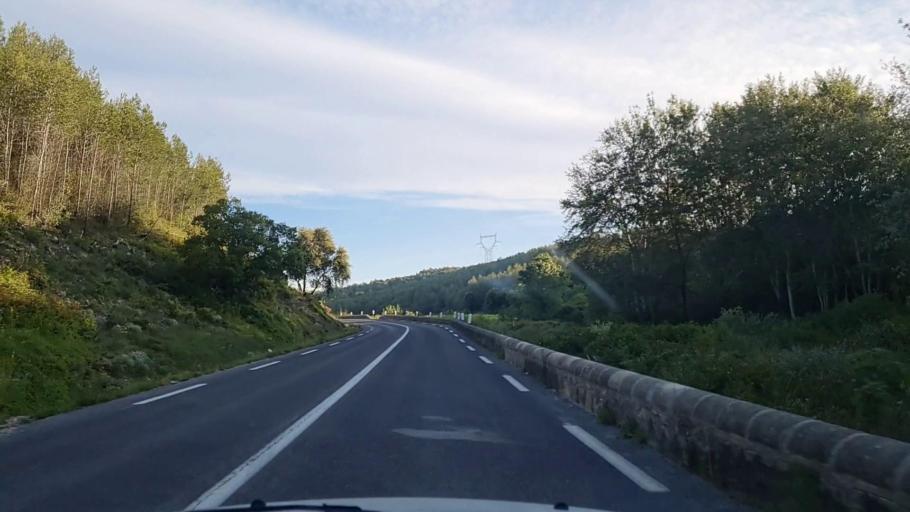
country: FR
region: Languedoc-Roussillon
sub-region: Departement du Gard
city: Villevieille
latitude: 43.8442
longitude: 4.0988
